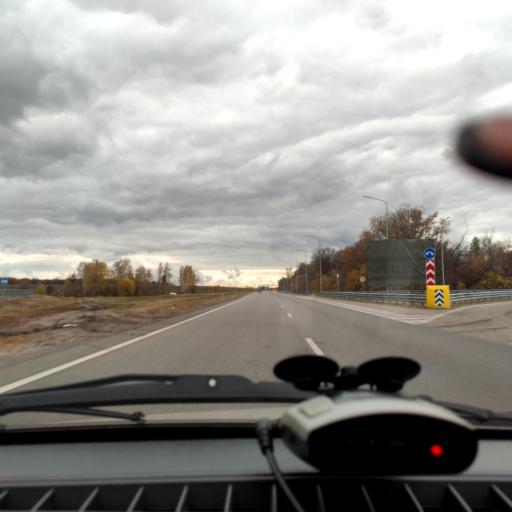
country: RU
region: Voronezj
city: Podgornoye
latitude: 51.8425
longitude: 39.2142
